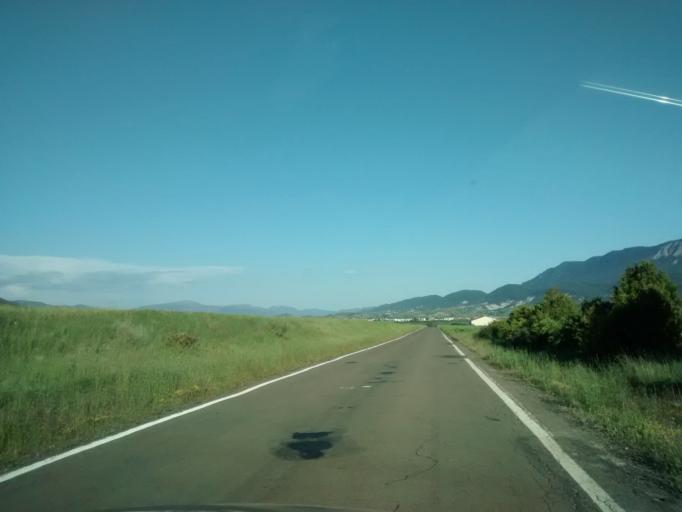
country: ES
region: Aragon
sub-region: Provincia de Huesca
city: Jaca
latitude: 42.5854
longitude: -0.6013
